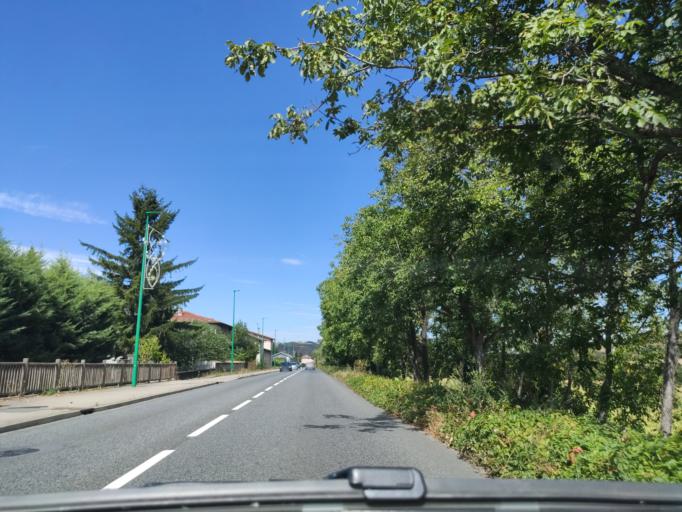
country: FR
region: Rhone-Alpes
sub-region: Departement de l'Isere
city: Reventin-Vaugris
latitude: 45.4753
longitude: 4.8293
